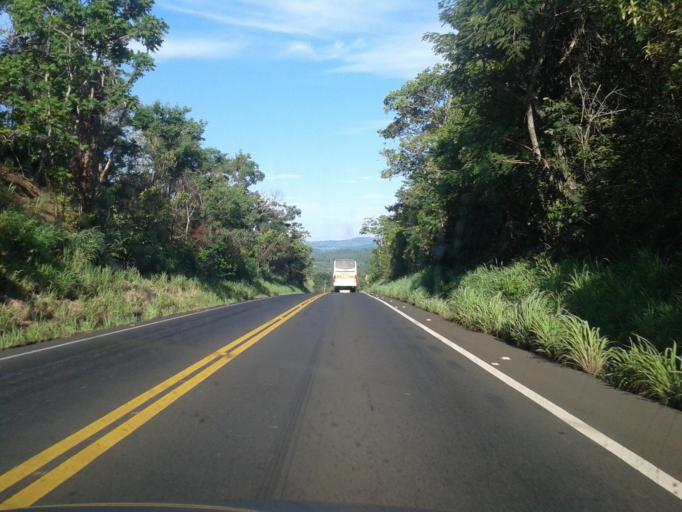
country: BR
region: Goias
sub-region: Caldas Novas
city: Caldas Novas
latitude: -18.1168
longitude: -48.6011
